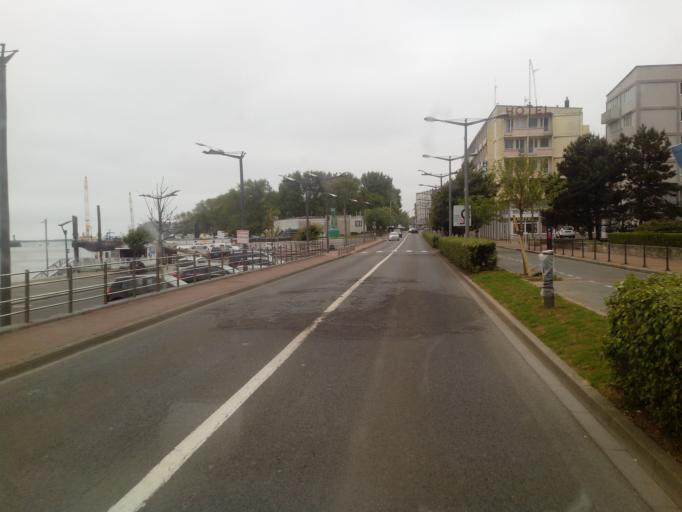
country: FR
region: Nord-Pas-de-Calais
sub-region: Departement du Pas-de-Calais
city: Saint-Martin-Boulogne
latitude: 50.7272
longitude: 1.5993
